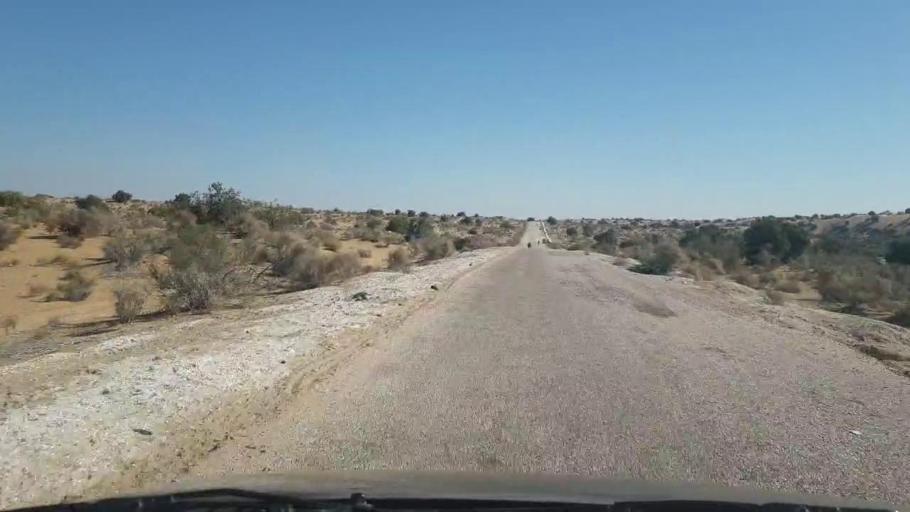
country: PK
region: Sindh
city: Bozdar
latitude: 27.0046
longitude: 68.8783
